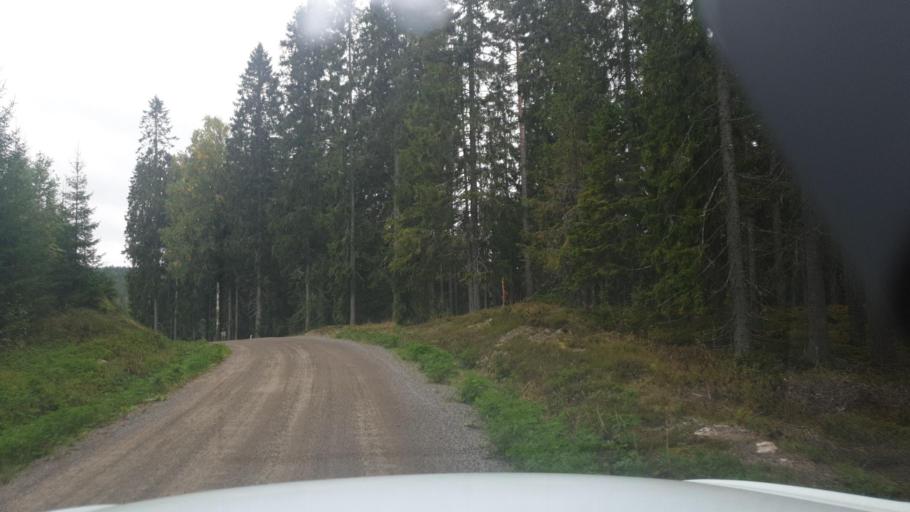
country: SE
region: Vaermland
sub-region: Sunne Kommun
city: Sunne
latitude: 59.8553
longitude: 12.8469
